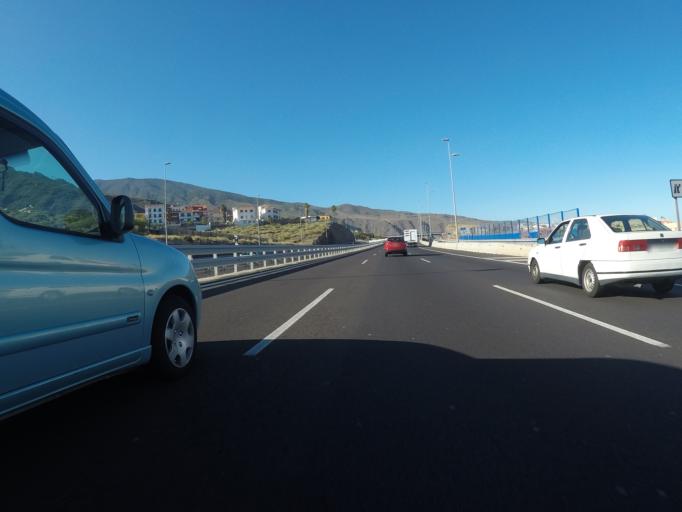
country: ES
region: Canary Islands
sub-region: Provincia de Santa Cruz de Tenerife
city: Candelaria
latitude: 28.3563
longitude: -16.3729
